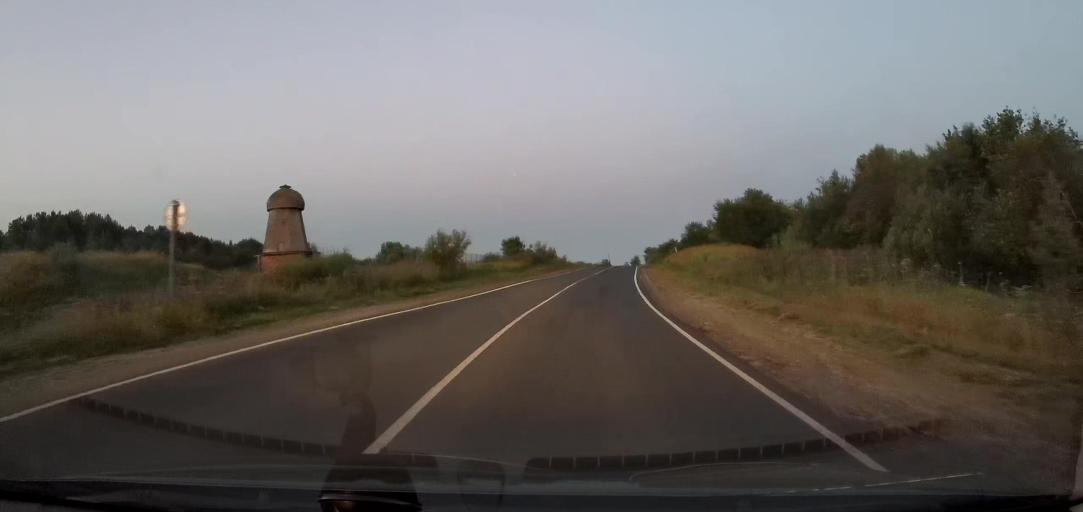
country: RU
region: Arkhangelskaya
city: Uyemskiy
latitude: 64.4496
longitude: 40.9441
